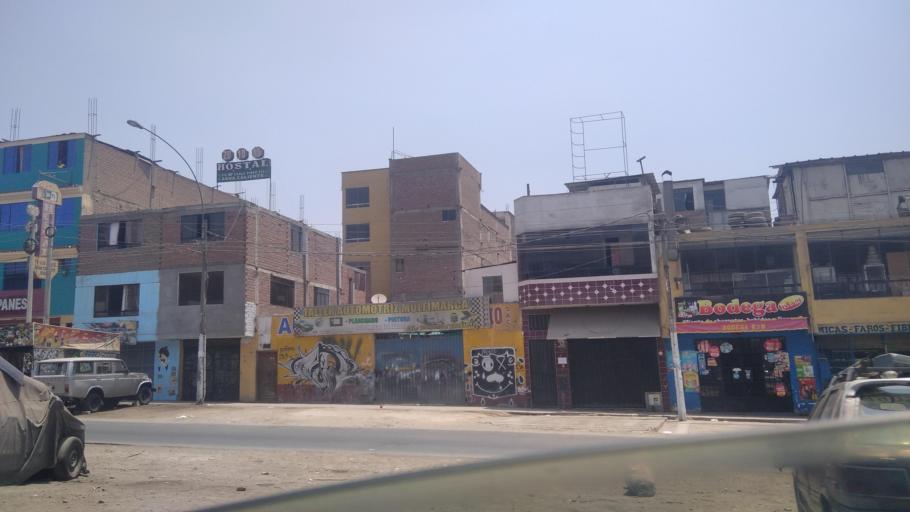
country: PE
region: Lima
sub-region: Lima
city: Independencia
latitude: -11.9728
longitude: -76.9970
